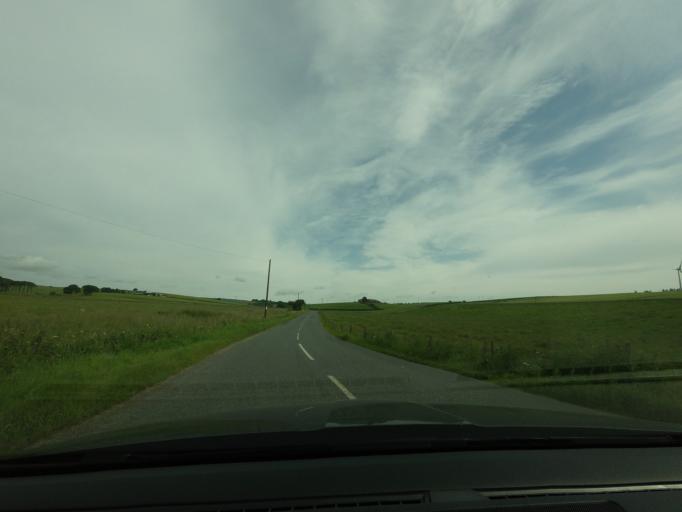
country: GB
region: Scotland
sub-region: Aberdeenshire
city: Turriff
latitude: 57.5589
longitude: -2.3090
